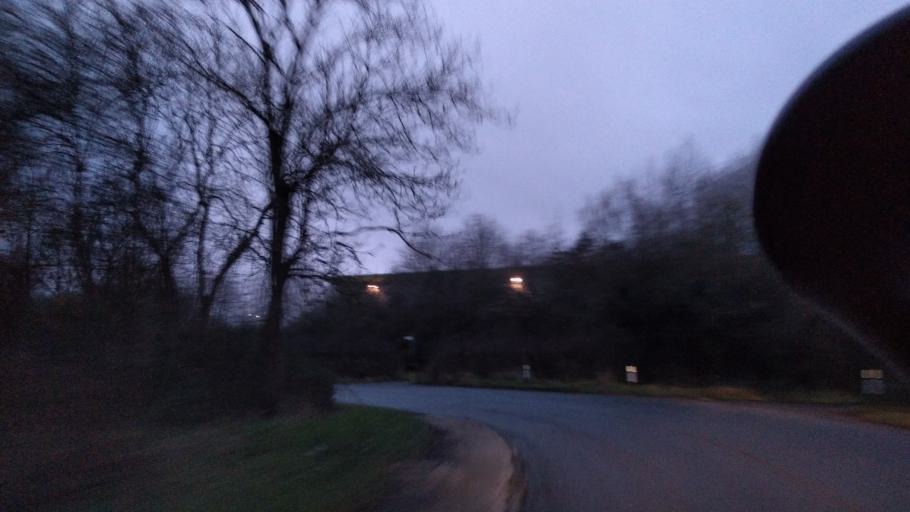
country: GB
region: England
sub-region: Borough of Swindon
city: Highworth
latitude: 51.5859
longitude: -1.7295
